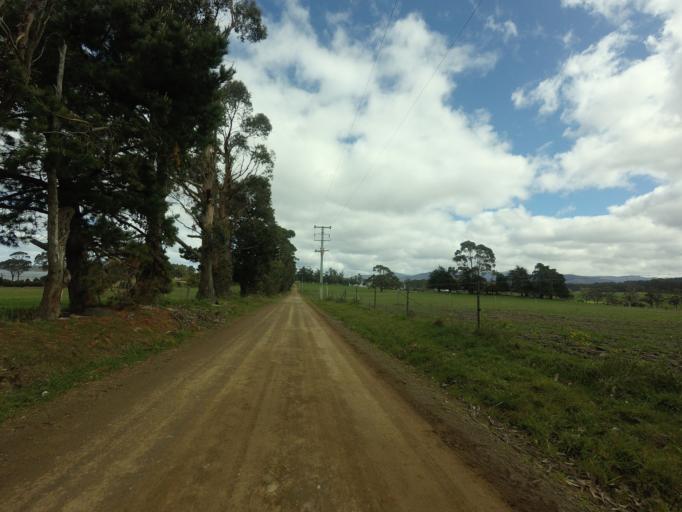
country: AU
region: Tasmania
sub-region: Huon Valley
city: Geeveston
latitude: -43.4313
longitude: 146.9902
